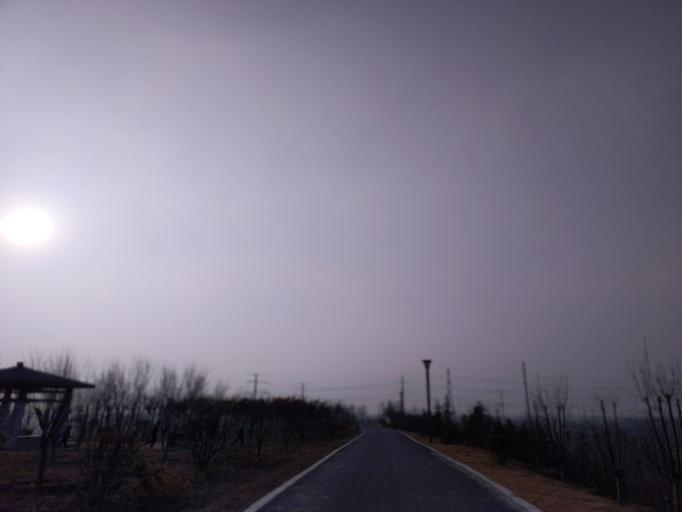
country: CN
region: Henan Sheng
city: Puyang
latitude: 35.8203
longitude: 115.0025
